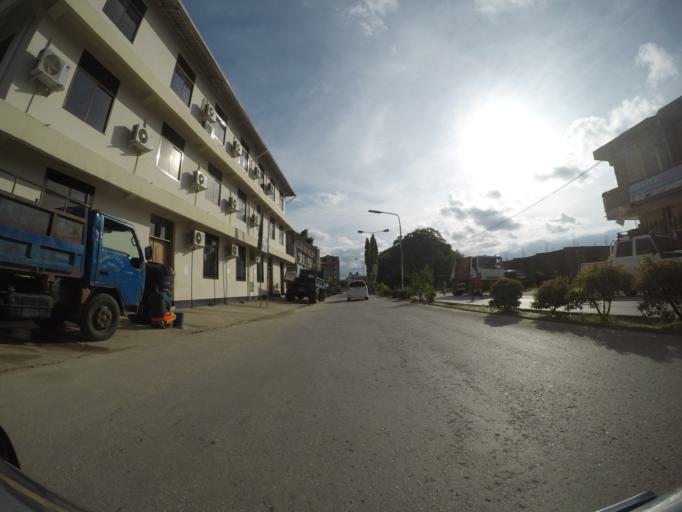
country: TZ
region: Pemba South
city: Chake Chake
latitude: -5.2408
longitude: 39.7692
